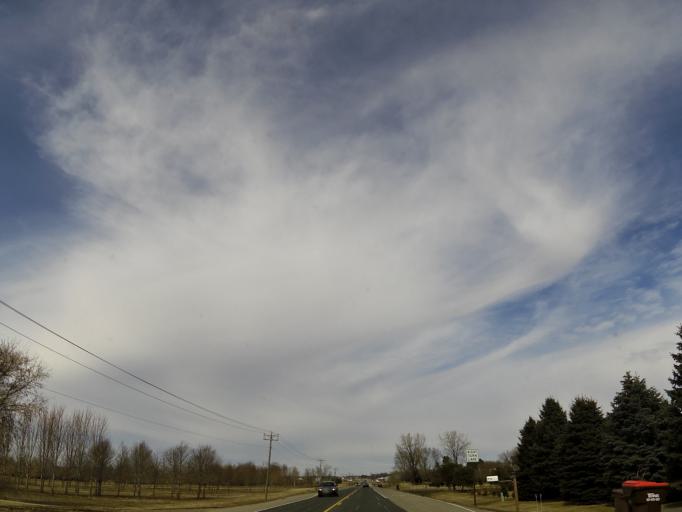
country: US
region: Minnesota
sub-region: Washington County
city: Lake Elmo
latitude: 44.9870
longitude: -92.8628
